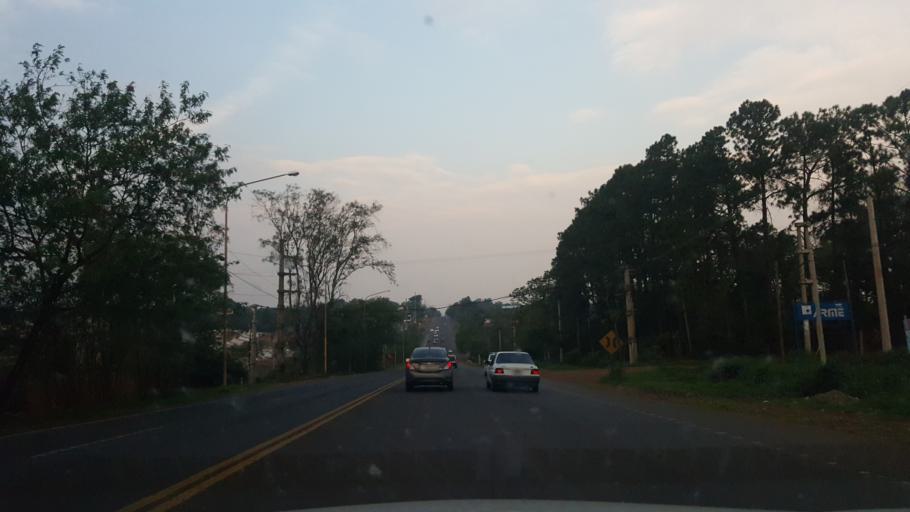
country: AR
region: Misiones
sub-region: Departamento de Capital
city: Posadas
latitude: -27.3994
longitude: -55.9484
